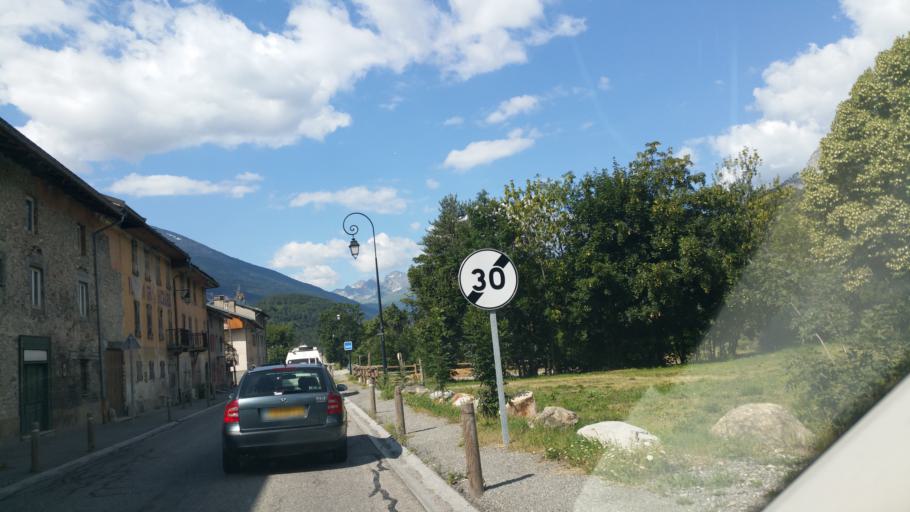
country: FR
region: Rhone-Alpes
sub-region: Departement de la Savoie
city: Modane
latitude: 45.2321
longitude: 6.7843
